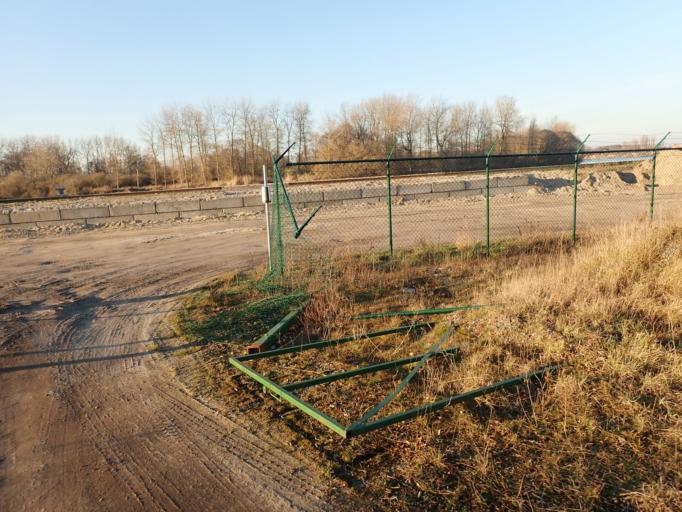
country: BE
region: Flanders
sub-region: Provincie Oost-Vlaanderen
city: Buggenhout
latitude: 51.0314
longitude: 4.1866
